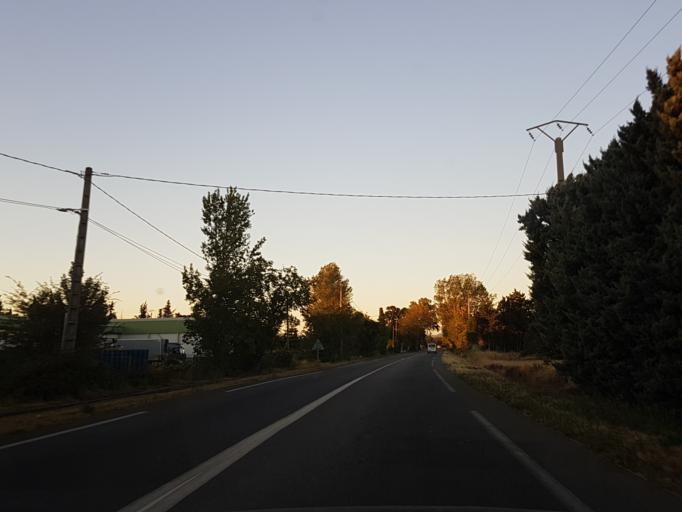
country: FR
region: Provence-Alpes-Cote d'Azur
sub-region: Departement du Vaucluse
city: Pernes-les-Fontaines
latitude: 44.0104
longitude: 5.0259
